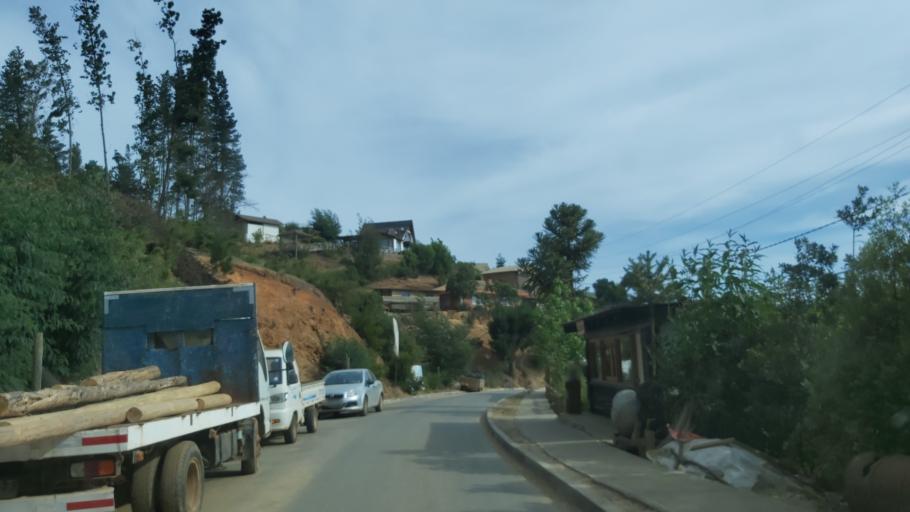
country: CL
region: Maule
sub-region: Provincia de Talca
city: Constitucion
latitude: -34.8472
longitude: -72.0390
